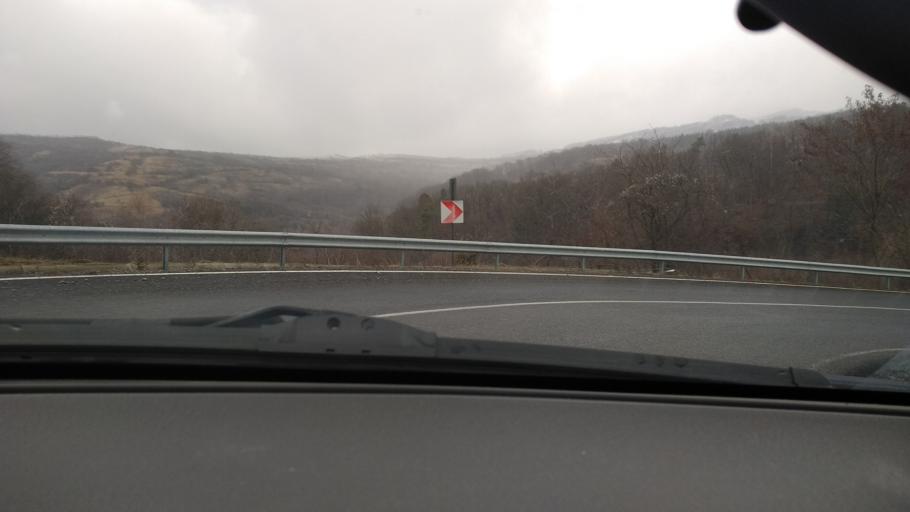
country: RO
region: Mures
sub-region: Comuna Magherani
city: Magherani
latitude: 46.5803
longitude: 24.9451
